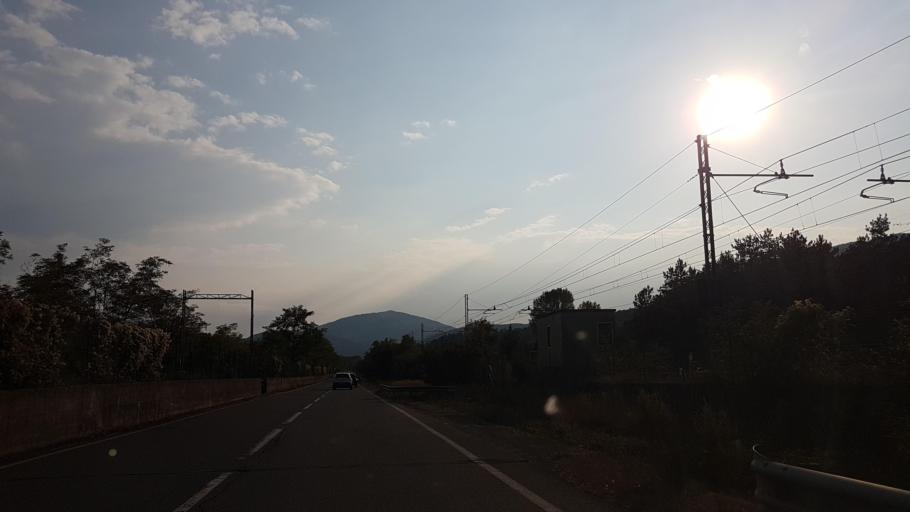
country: IT
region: Emilia-Romagna
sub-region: Provincia di Parma
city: Solignano
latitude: 44.6039
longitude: 9.9724
